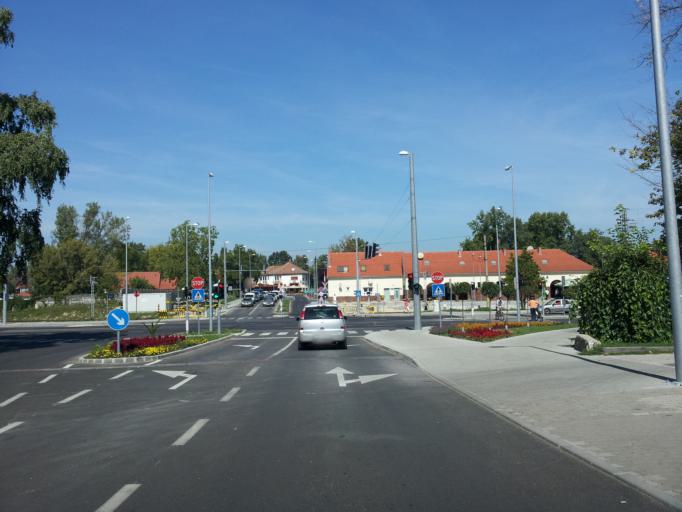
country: HU
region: Somogy
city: Zamardi
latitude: 46.8793
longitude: 17.9450
